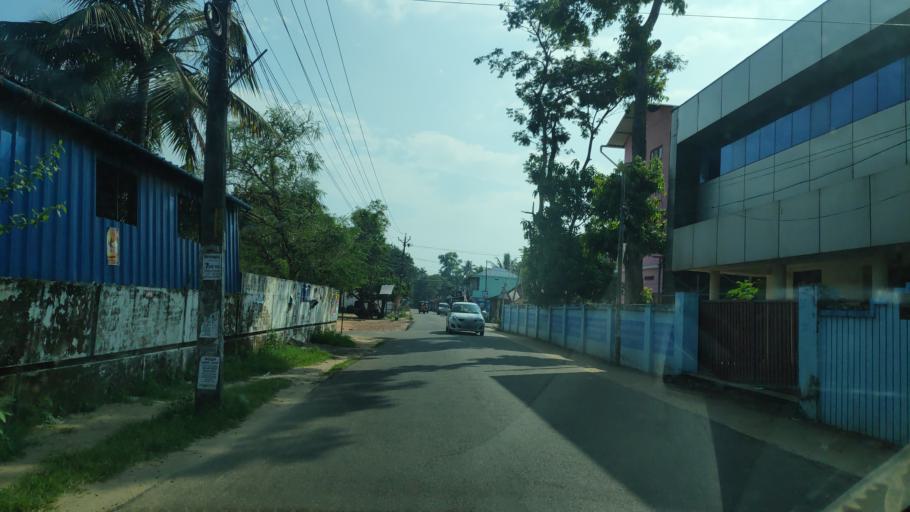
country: IN
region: Kerala
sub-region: Alappuzha
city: Alleppey
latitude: 9.5650
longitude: 76.3091
